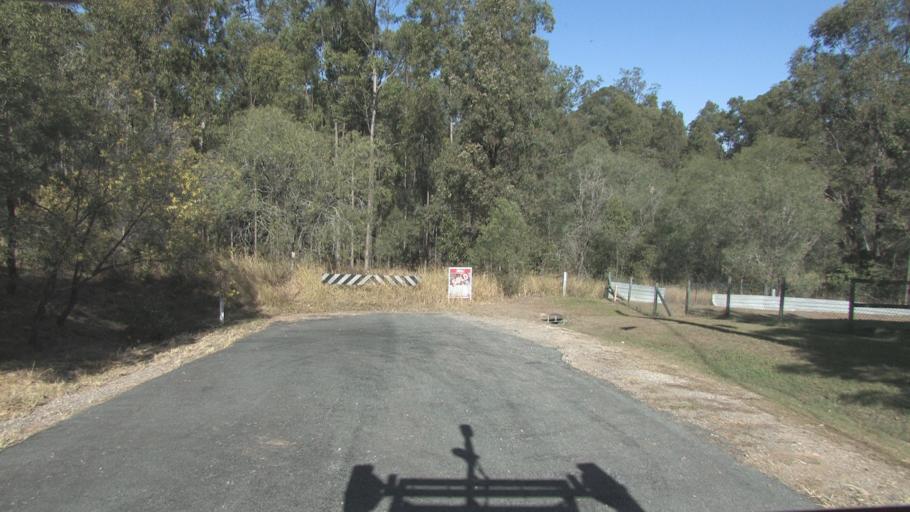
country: AU
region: Queensland
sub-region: Logan
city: Cedar Vale
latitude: -27.8578
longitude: 152.9863
